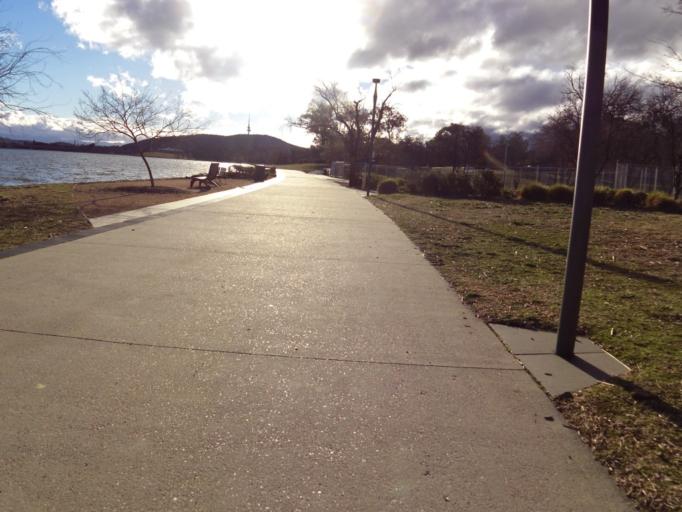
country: AU
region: Australian Capital Territory
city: Canberra
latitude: -35.2930
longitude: 149.1413
